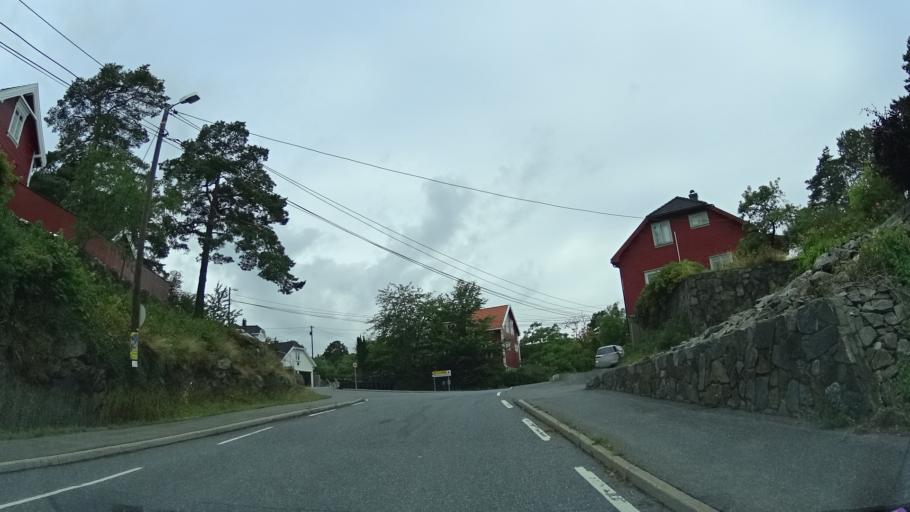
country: NO
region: Aust-Agder
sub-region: Arendal
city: Arendal
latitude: 58.4514
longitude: 8.7635
